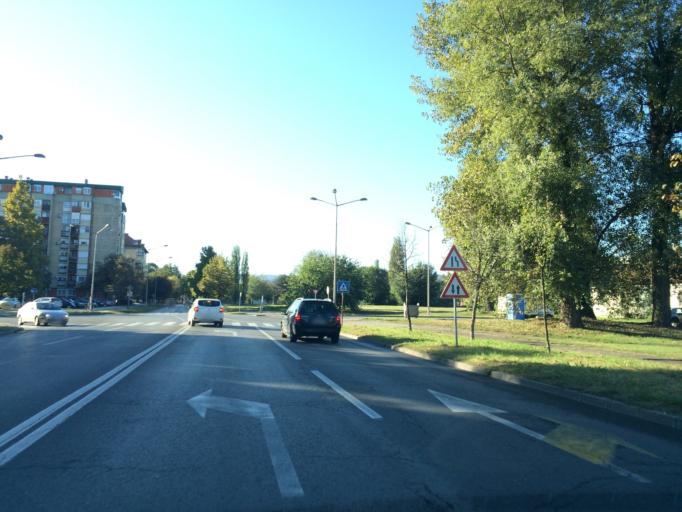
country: RS
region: Autonomna Pokrajina Vojvodina
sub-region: Juznobacki Okrug
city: Novi Sad
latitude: 45.2377
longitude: 19.8263
